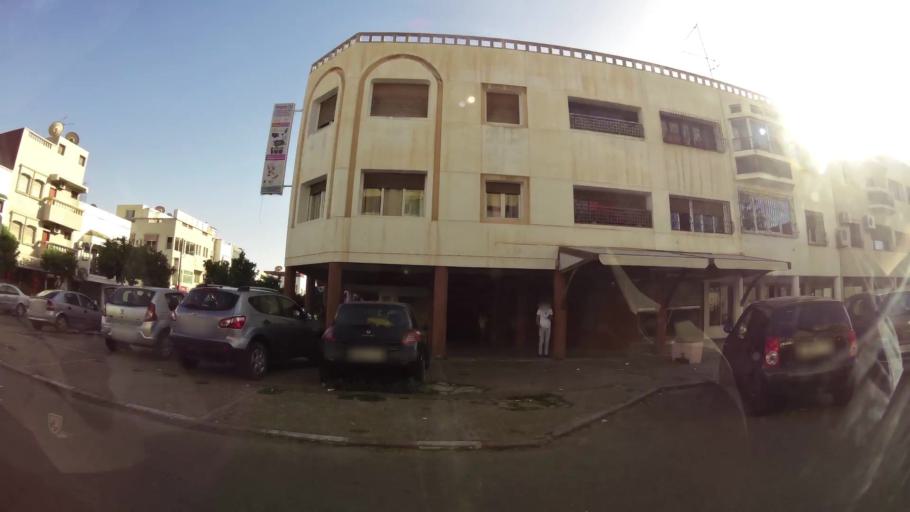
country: MA
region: Souss-Massa-Draa
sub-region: Agadir-Ida-ou-Tnan
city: Agadir
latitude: 30.4299
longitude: -9.5813
